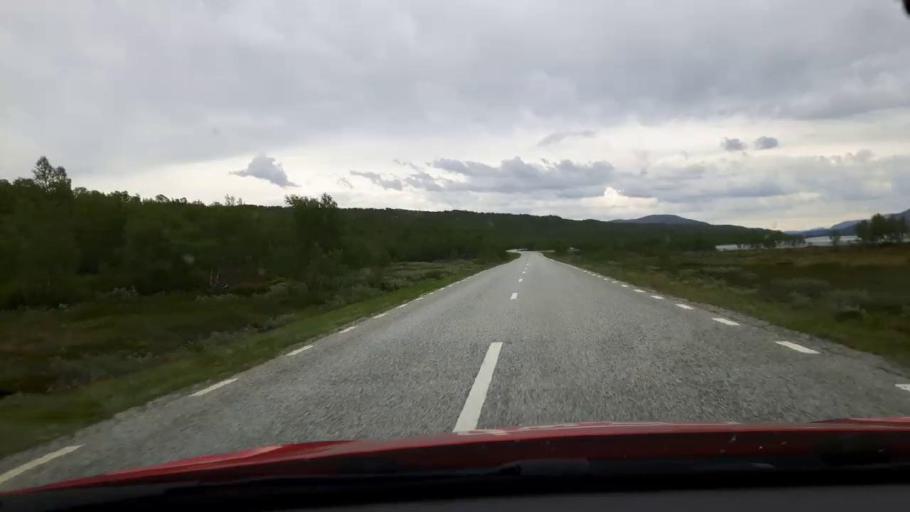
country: NO
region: Sor-Trondelag
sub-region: Tydal
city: Aas
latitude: 62.6158
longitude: 12.1392
